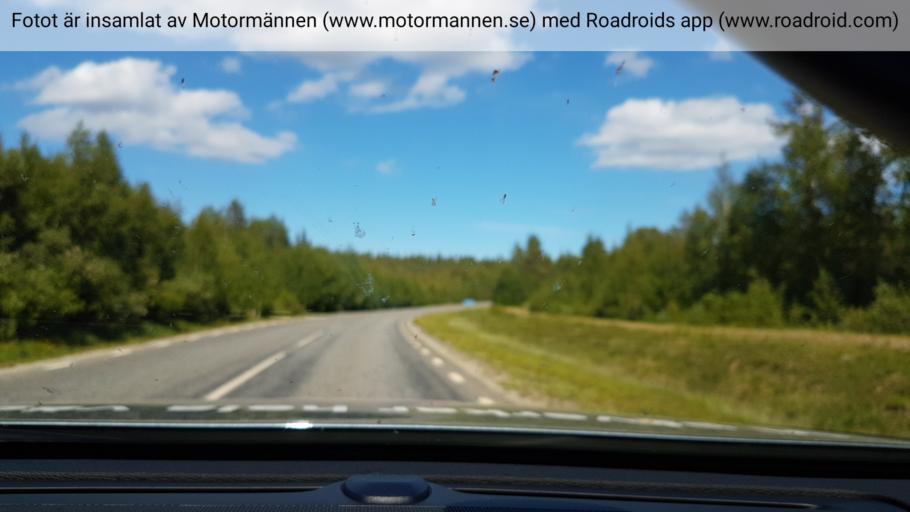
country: SE
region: Vaesterbotten
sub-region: Lycksele Kommun
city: Lycksele
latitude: 64.5874
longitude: 18.5777
